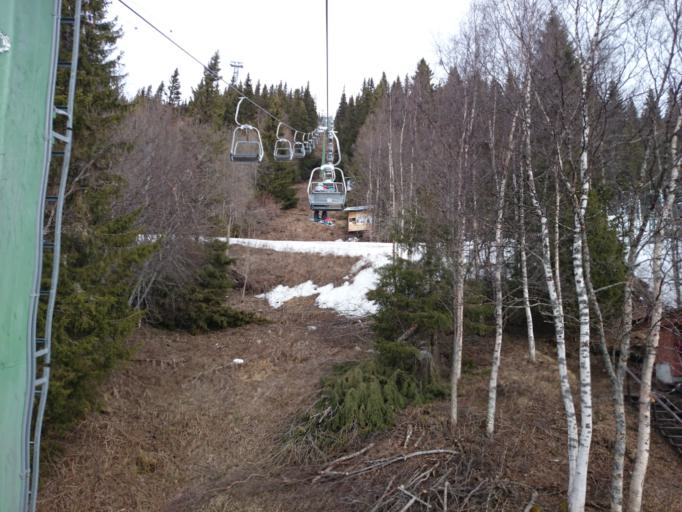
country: SE
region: Jaemtland
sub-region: Are Kommun
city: Are
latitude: 63.4040
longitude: 13.0773
